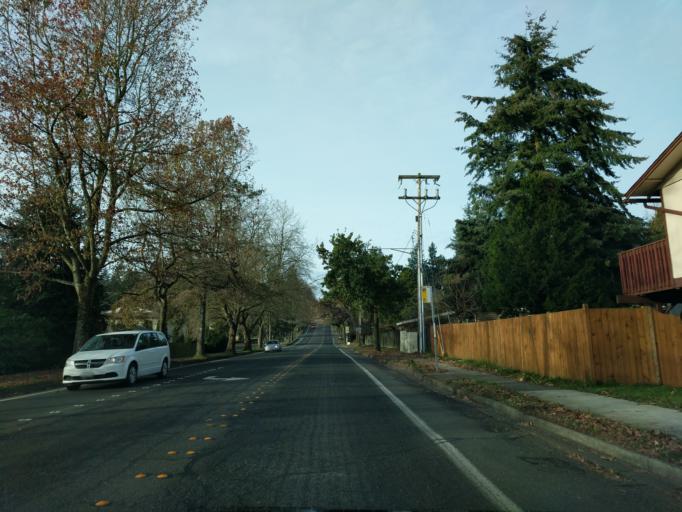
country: US
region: Washington
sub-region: King County
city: Shoreline
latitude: 47.7415
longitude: -122.3347
